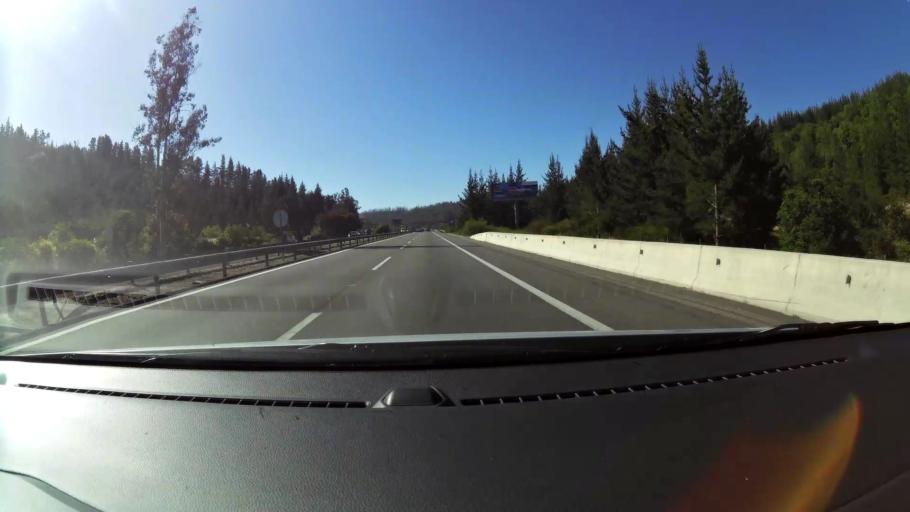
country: CL
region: Valparaiso
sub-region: Provincia de Marga Marga
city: Quilpue
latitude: -33.2233
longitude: -71.4698
